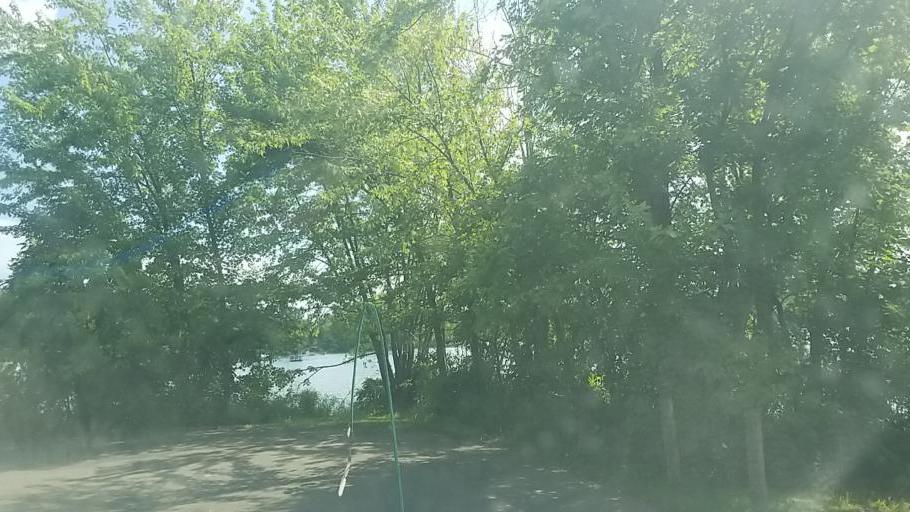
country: US
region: Ohio
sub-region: Ashland County
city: Loudonville
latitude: 40.6429
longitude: -82.3453
